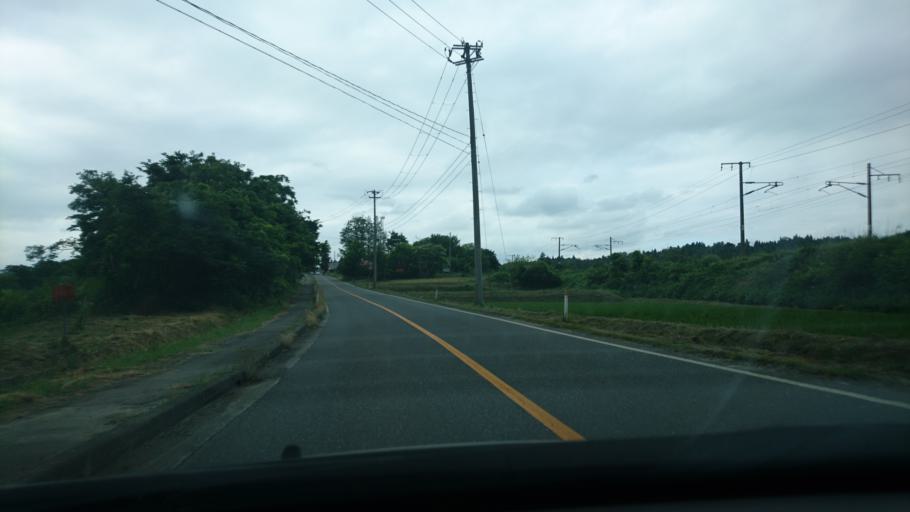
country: JP
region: Iwate
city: Ichinoseki
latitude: 38.8171
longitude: 141.1816
